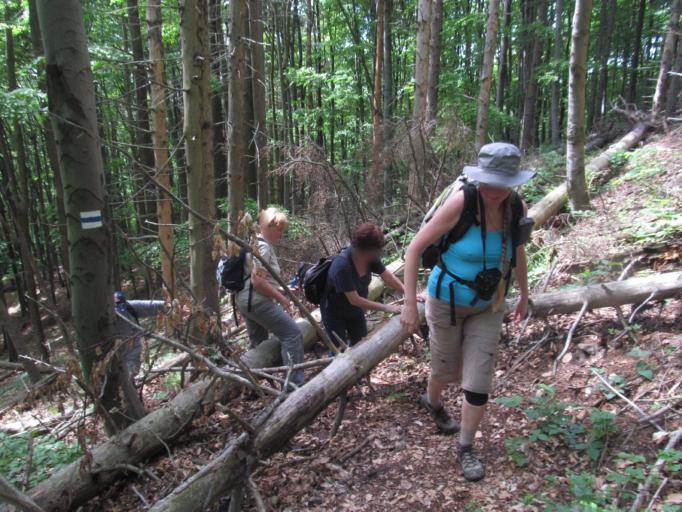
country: HU
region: Borsod-Abauj-Zemplen
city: Gonc
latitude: 48.5729
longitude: 21.4602
